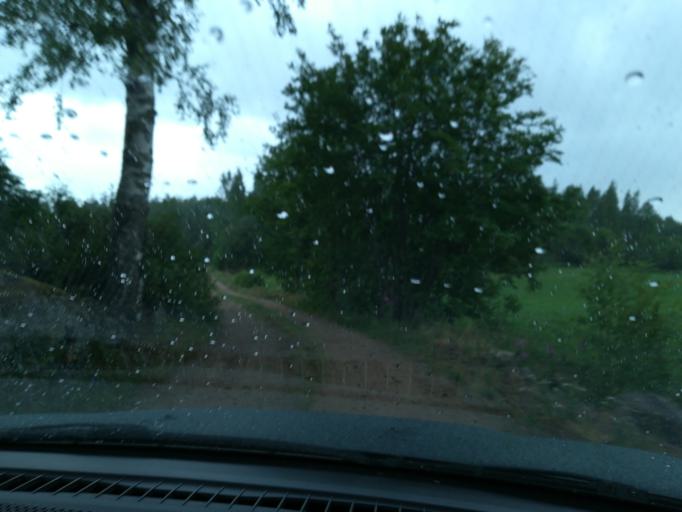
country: FI
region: South Karelia
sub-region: Lappeenranta
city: Savitaipale
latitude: 61.1804
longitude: 27.5482
